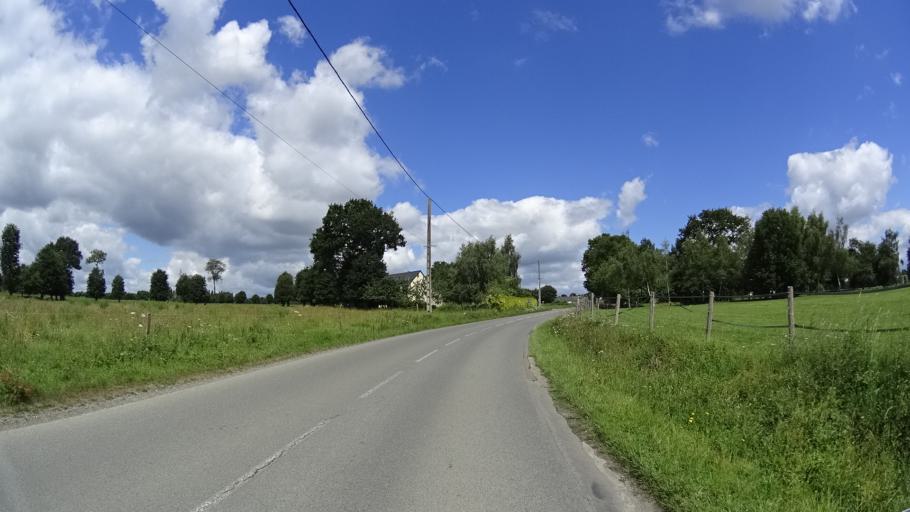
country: FR
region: Brittany
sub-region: Departement d'Ille-et-Vilaine
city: Saint-Gilles
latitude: 48.1378
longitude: -1.8275
